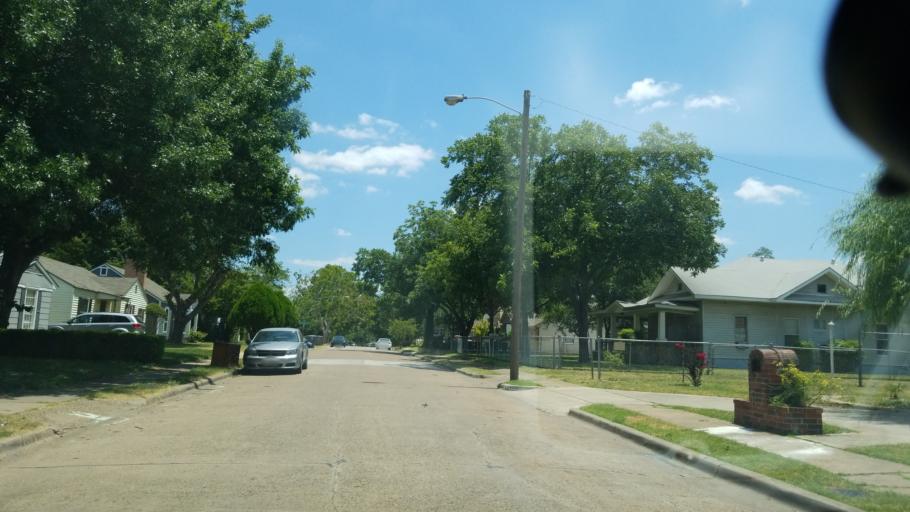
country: US
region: Texas
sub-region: Dallas County
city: Cockrell Hill
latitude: 32.7214
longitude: -96.8474
